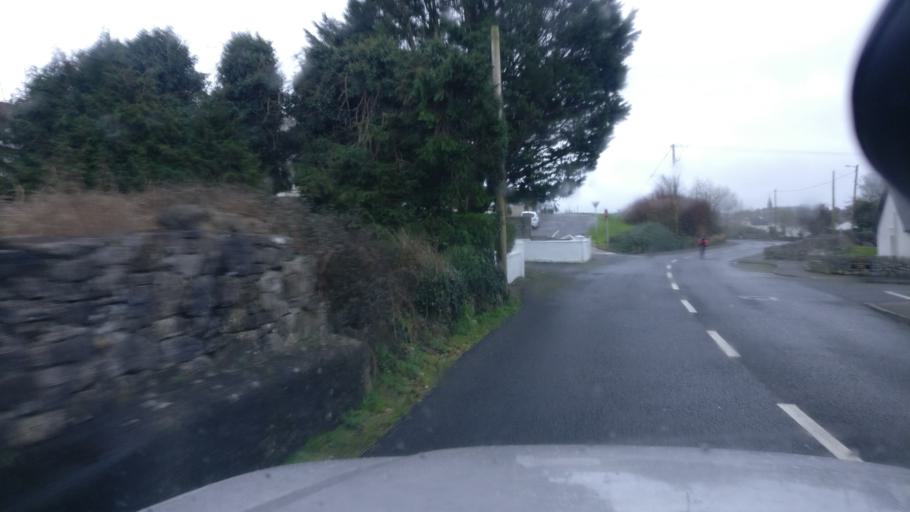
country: IE
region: Connaught
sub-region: County Galway
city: Loughrea
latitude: 53.2030
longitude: -8.5608
